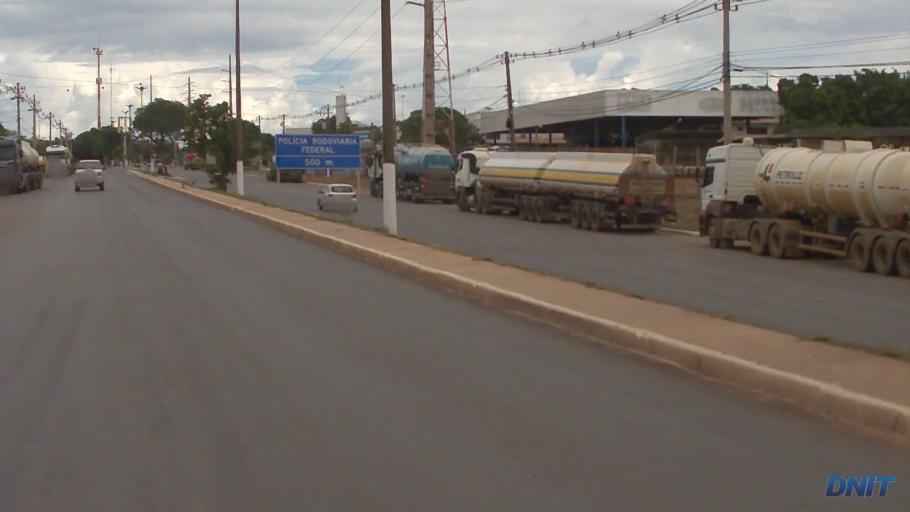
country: BR
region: Mato Grosso
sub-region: Varzea Grande
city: Varzea Grande
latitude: -15.6474
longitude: -56.1901
